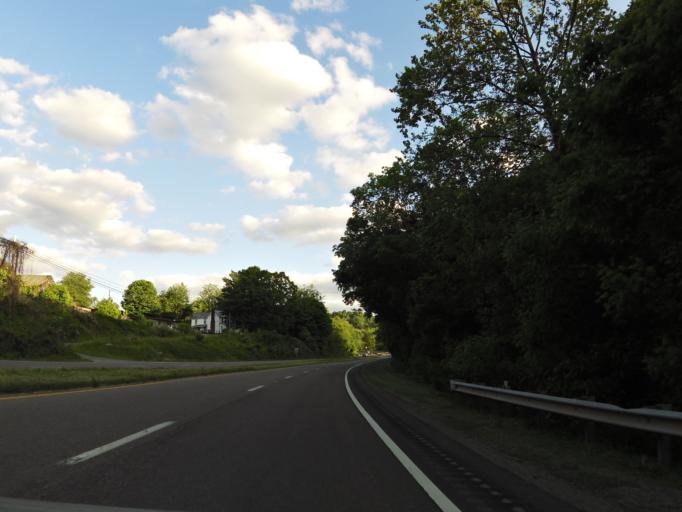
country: US
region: Virginia
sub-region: Washington County
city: Abingdon
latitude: 36.7356
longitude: -82.0375
